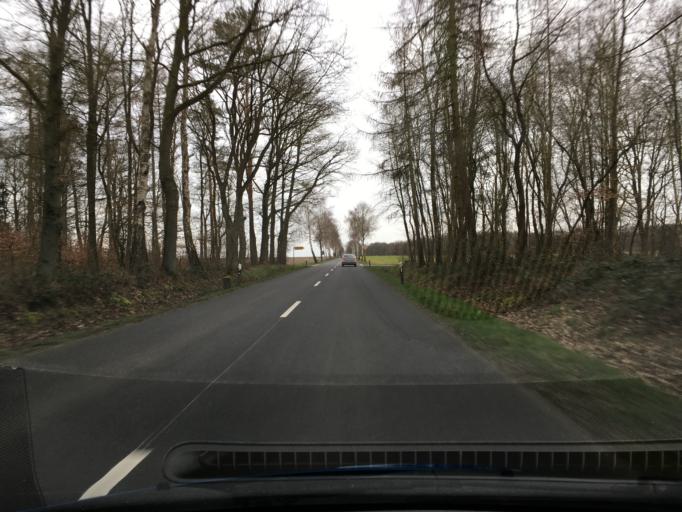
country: DE
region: Lower Saxony
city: Emmendorf
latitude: 53.0226
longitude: 10.6024
